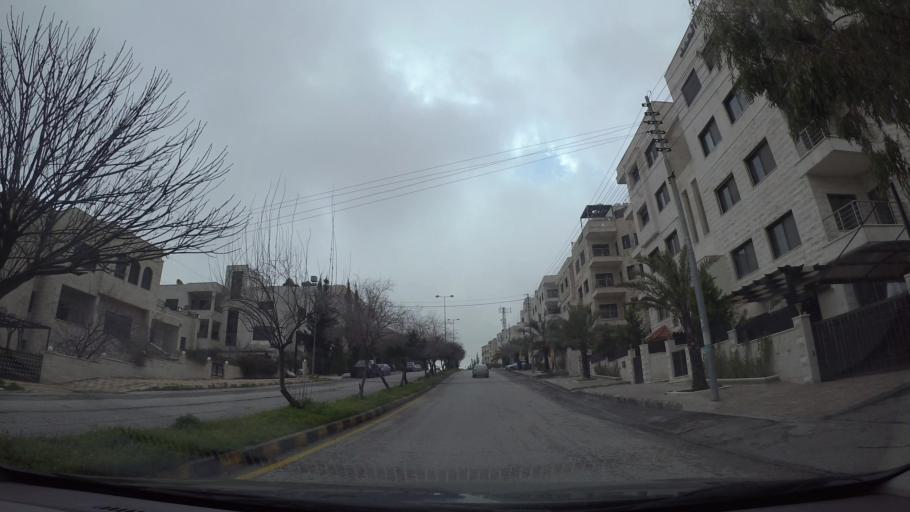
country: JO
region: Amman
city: Wadi as Sir
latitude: 31.9422
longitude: 35.8623
